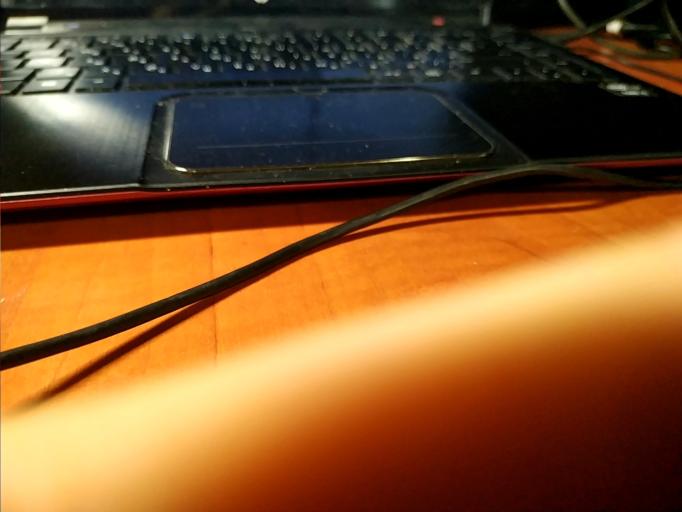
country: RU
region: Tverskaya
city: Rameshki
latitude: 57.1450
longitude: 36.0938
